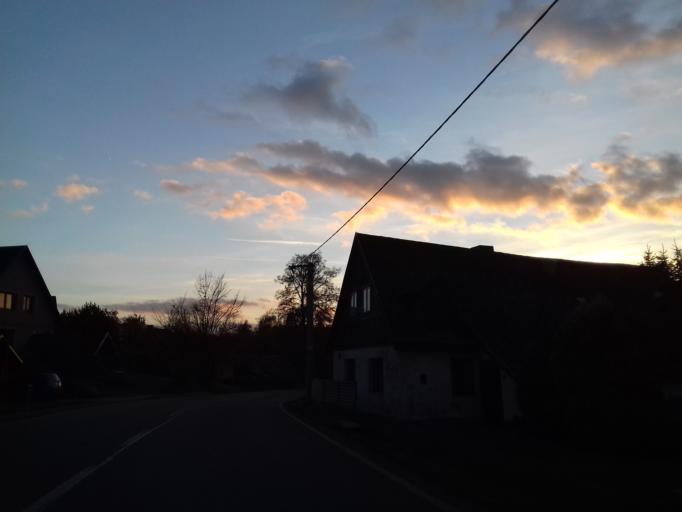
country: CZ
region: Vysocina
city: Krizova
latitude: 49.7180
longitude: 15.8607
